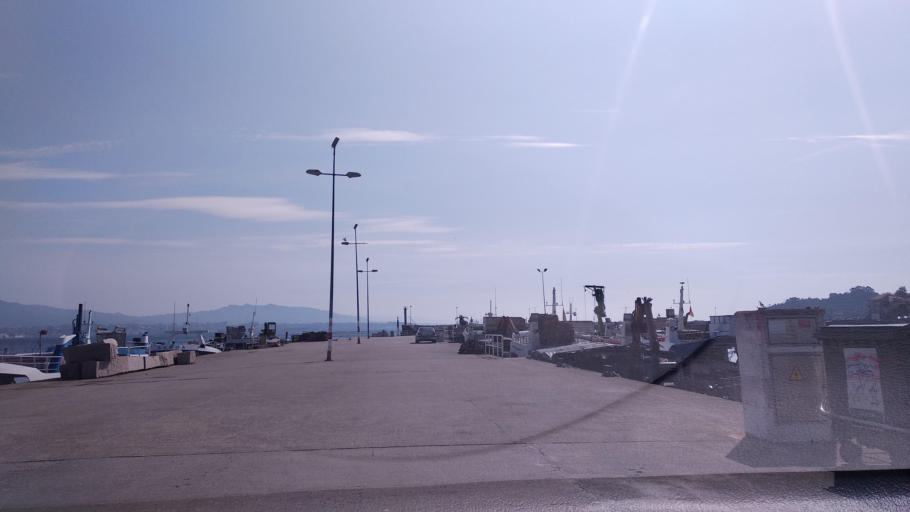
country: ES
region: Galicia
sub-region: Provincia de Pontevedra
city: Moana
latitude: 42.2730
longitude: -8.7360
